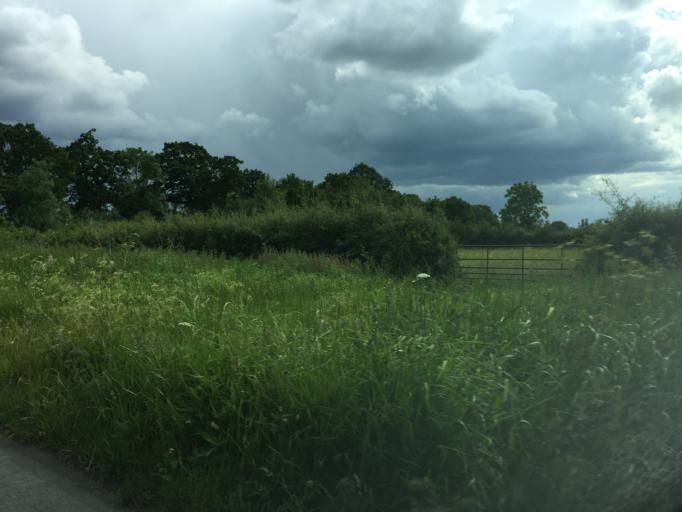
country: GB
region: England
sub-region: Wiltshire
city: Cricklade
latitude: 51.6232
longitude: -1.8559
